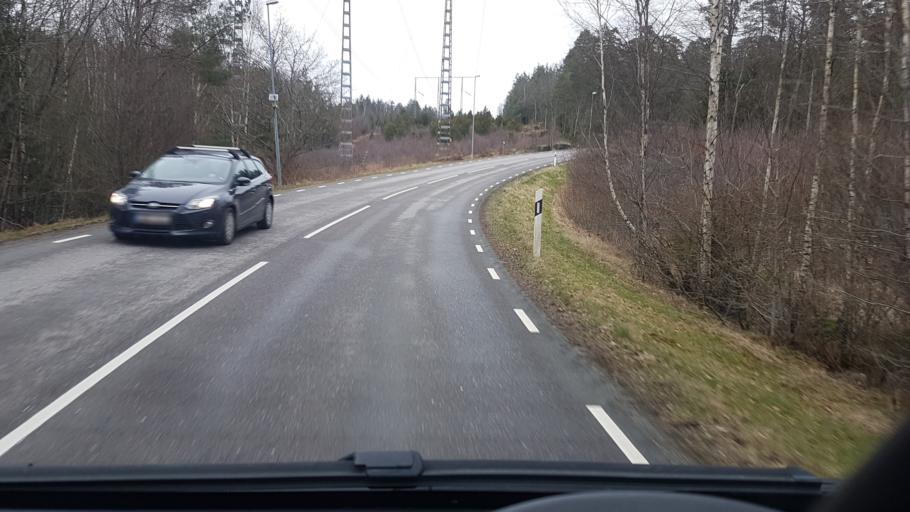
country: SE
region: Vaestra Goetaland
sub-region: Lerums Kommun
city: Stenkullen
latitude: 57.8081
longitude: 12.3346
